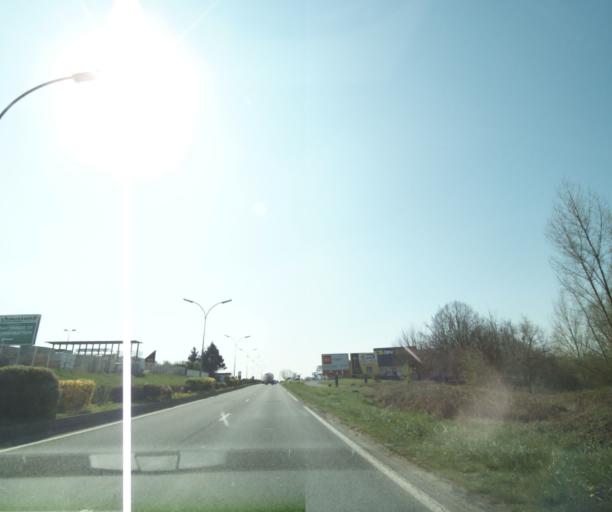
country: FR
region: Midi-Pyrenees
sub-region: Departement de l'Aveyron
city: Olemps
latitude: 44.3719
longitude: 2.5471
